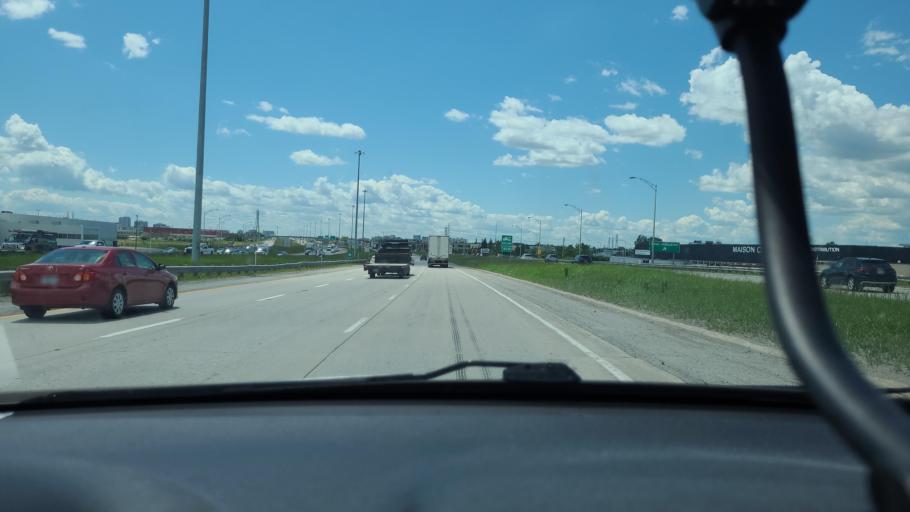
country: CA
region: Quebec
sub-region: Laval
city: Laval
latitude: 45.5884
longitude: -73.7304
